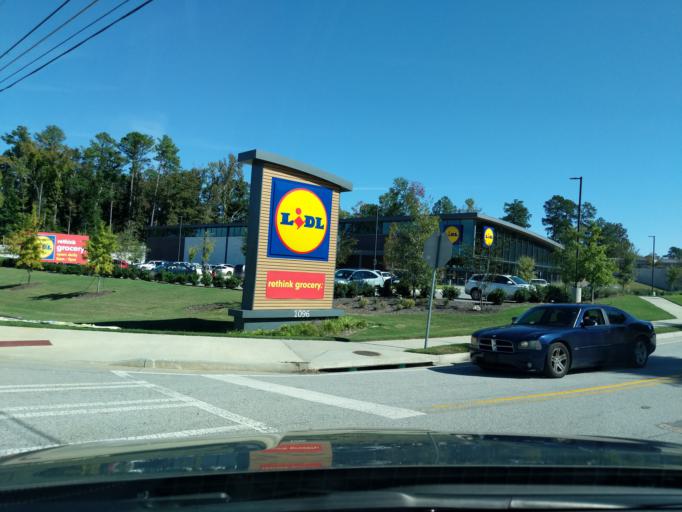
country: US
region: Georgia
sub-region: Columbia County
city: Martinez
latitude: 33.5109
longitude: -82.0276
